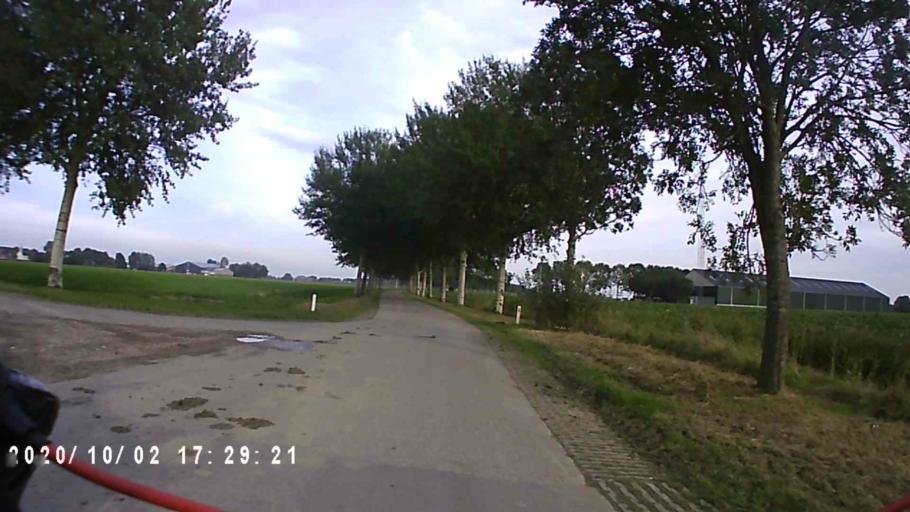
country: NL
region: Groningen
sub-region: Gemeente De Marne
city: Ulrum
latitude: 53.3374
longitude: 6.3215
